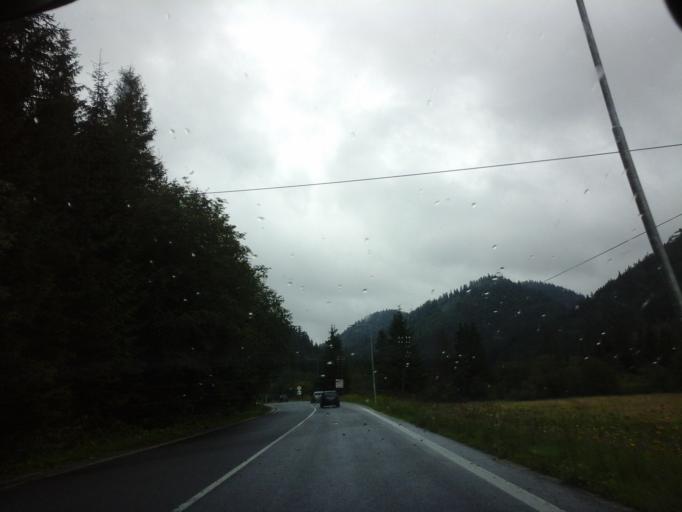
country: SK
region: Kosicky
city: Dobsina
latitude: 48.8739
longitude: 20.2999
